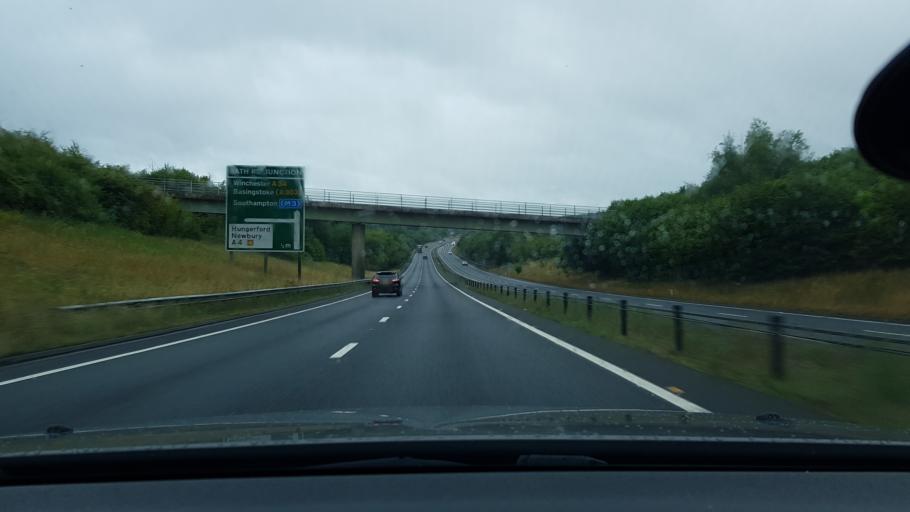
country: GB
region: England
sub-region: West Berkshire
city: Winterbourne
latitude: 51.4216
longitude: -1.3449
